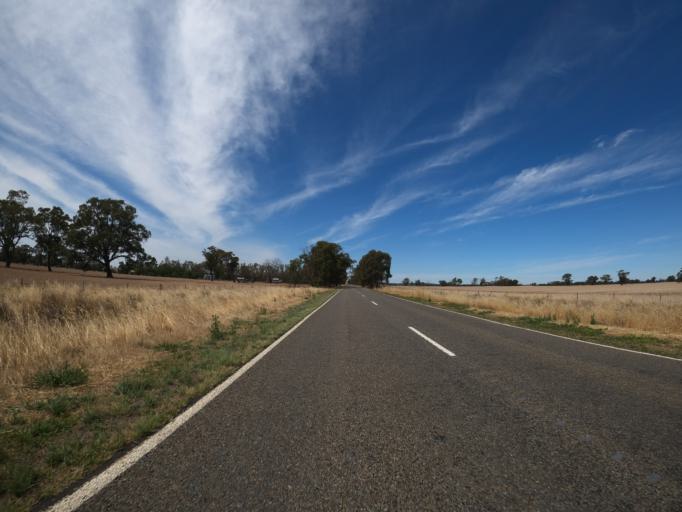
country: AU
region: Victoria
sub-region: Benalla
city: Benalla
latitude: -36.2896
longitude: 145.9523
